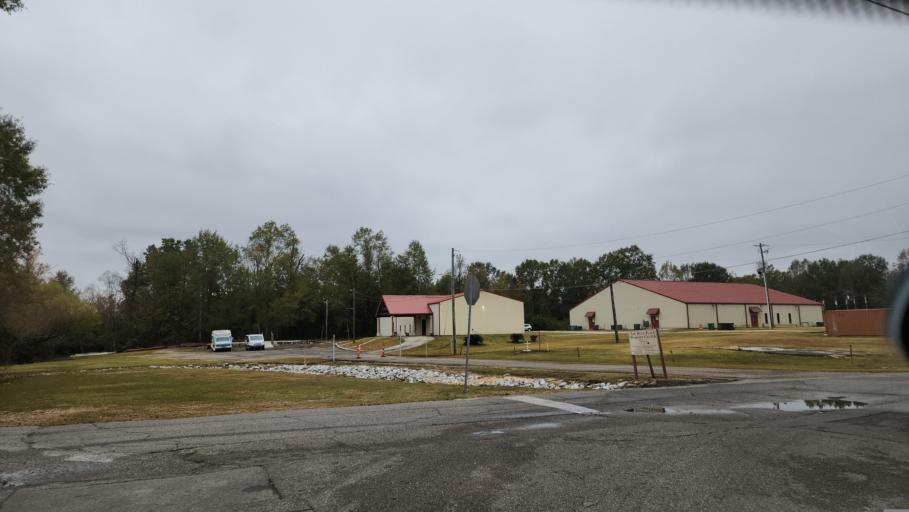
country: US
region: Mississippi
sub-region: Forrest County
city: Hattiesburg
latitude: 31.3031
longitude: -89.2995
